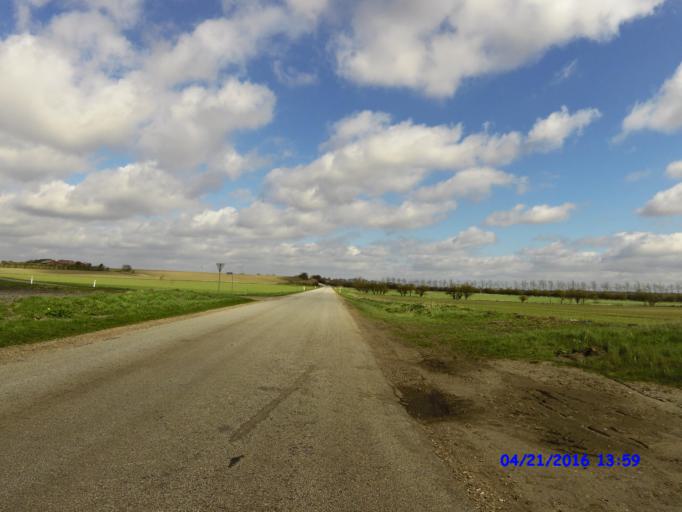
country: DK
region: South Denmark
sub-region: Haderslev Kommune
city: Gram
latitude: 55.2530
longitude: 9.0674
